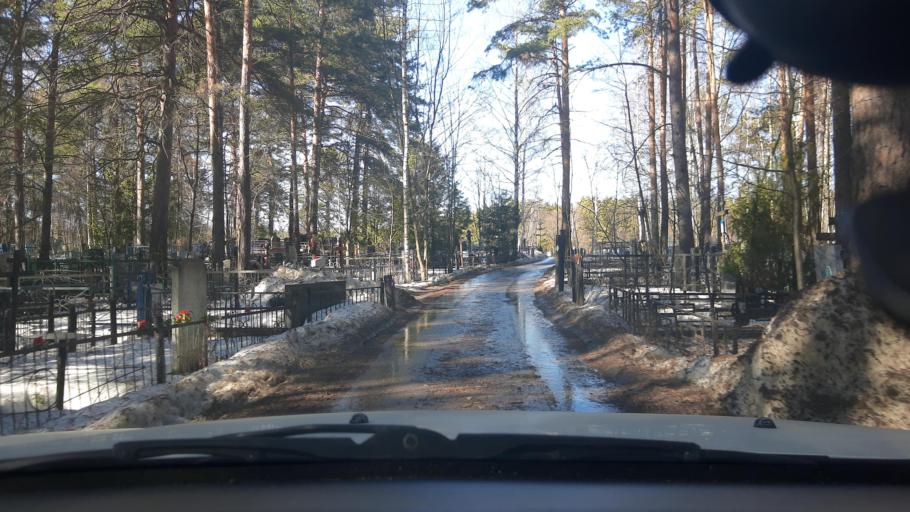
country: RU
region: Nizjnij Novgorod
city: Pyra
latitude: 56.2422
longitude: 43.3706
